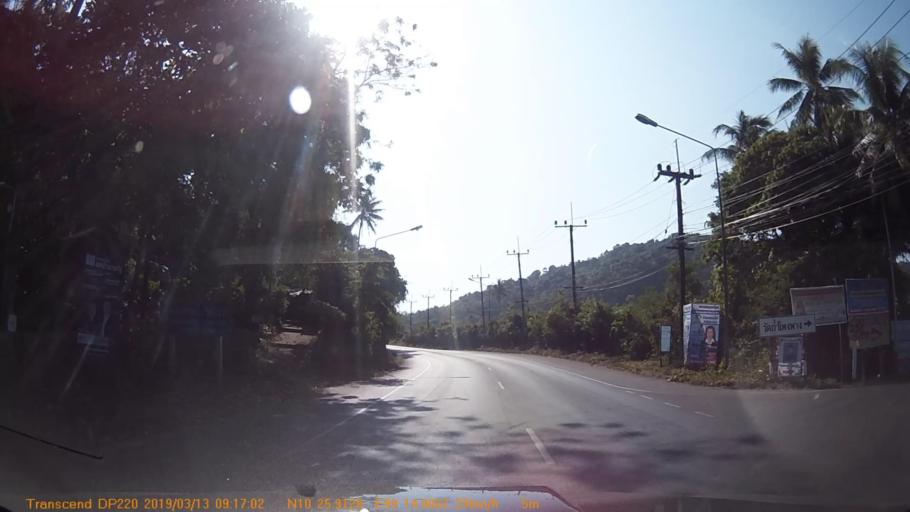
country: TH
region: Chumphon
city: Chumphon
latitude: 10.4319
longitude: 99.2485
